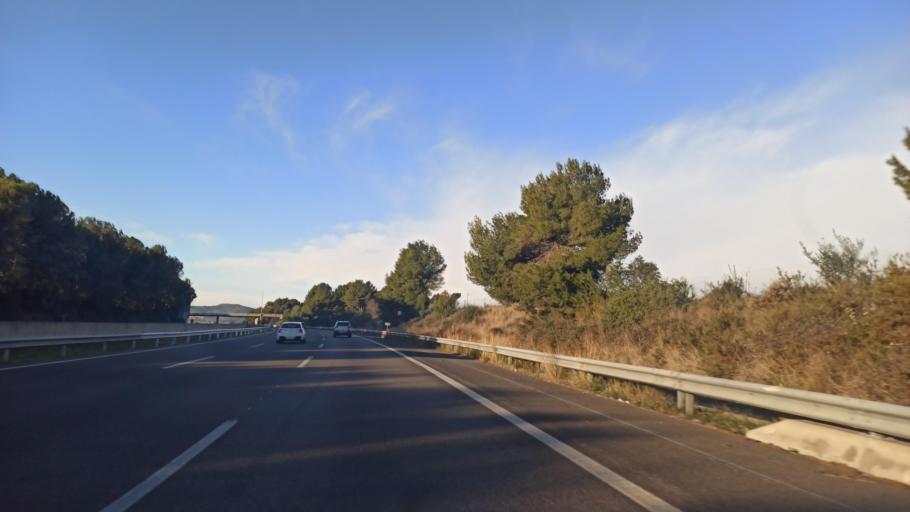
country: ES
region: Catalonia
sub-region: Provincia de Tarragona
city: Sant Jaume dels Domenys
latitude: 41.2882
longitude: 1.5835
